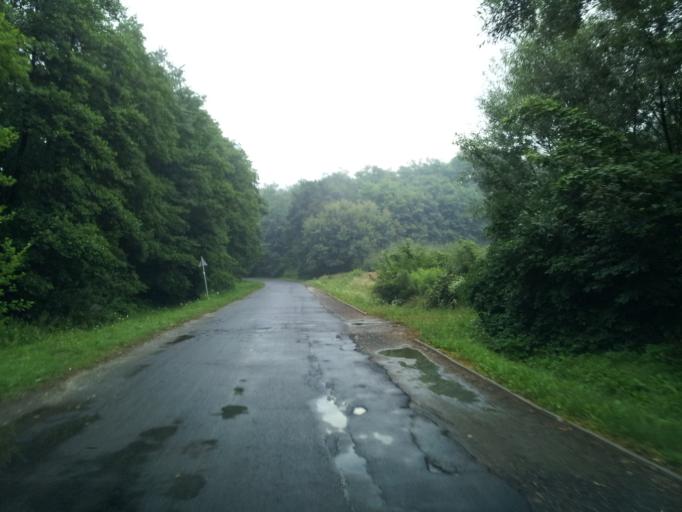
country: HU
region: Zala
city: Zalalovo
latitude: 46.8721
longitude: 16.5502
